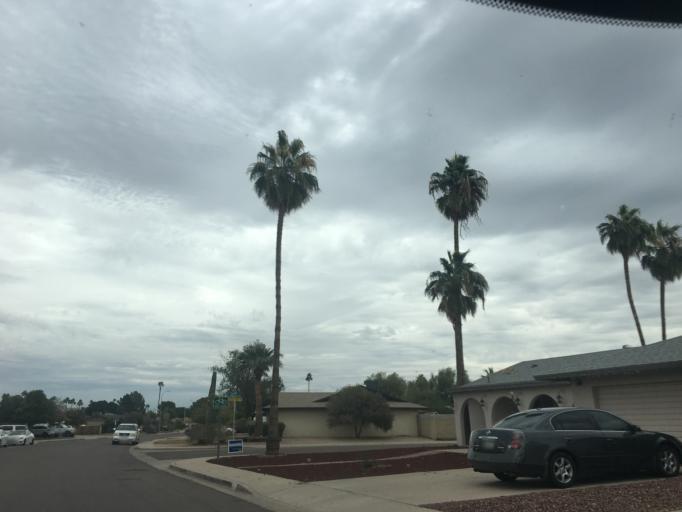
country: US
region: Arizona
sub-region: Maricopa County
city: Guadalupe
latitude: 33.3694
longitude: -111.9283
